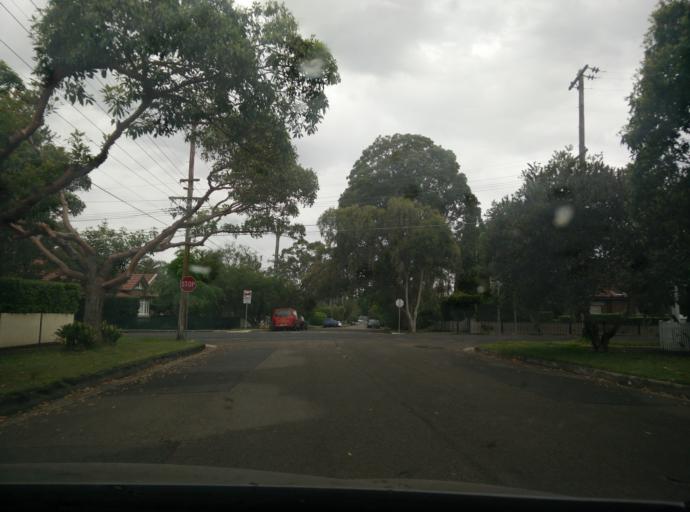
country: AU
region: New South Wales
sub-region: Ku-ring-gai
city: Roseville Chase
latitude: -33.7815
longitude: 151.1919
